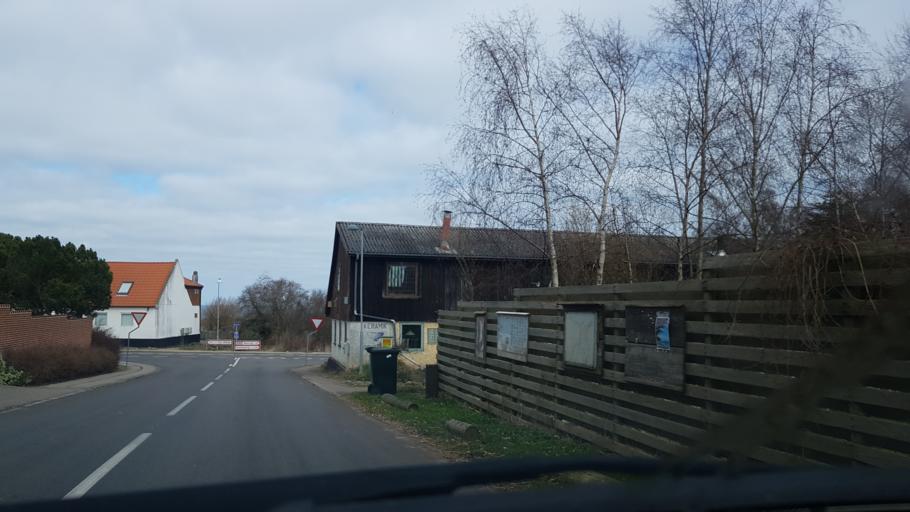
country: DK
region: Zealand
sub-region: Odsherred Kommune
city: Hojby
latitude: 55.9409
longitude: 11.5176
